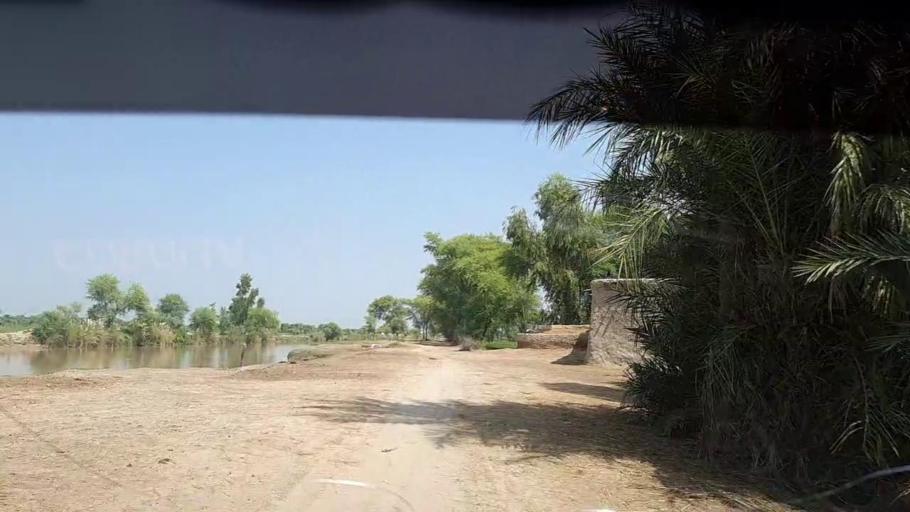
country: PK
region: Sindh
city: Tangwani
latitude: 28.2329
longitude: 68.9603
